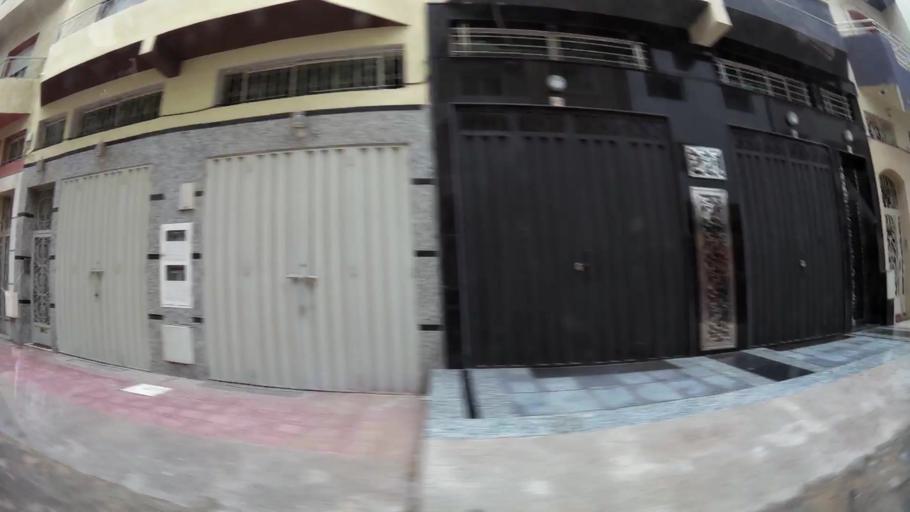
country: MA
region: Grand Casablanca
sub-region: Casablanca
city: Casablanca
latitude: 33.5352
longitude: -7.5980
